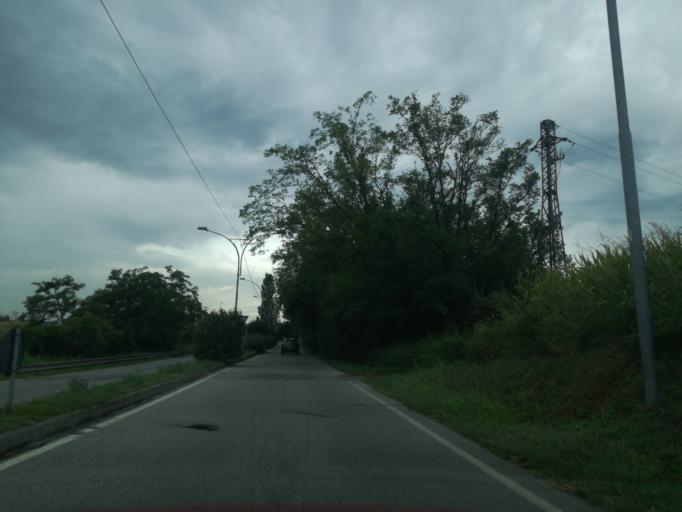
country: IT
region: Lombardy
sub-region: Provincia di Monza e Brianza
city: Mezzago
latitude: 45.6195
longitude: 9.4395
